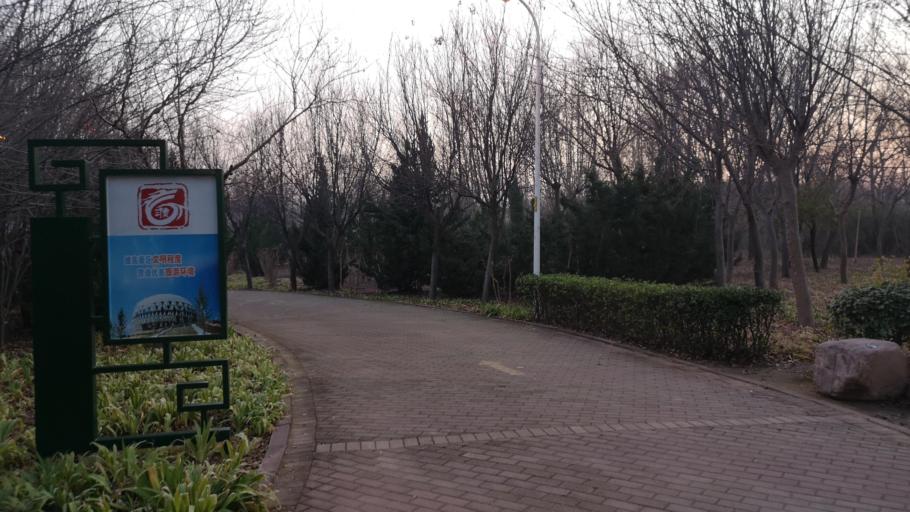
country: CN
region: Henan Sheng
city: Zhongyuanlu
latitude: 35.7429
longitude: 115.0609
